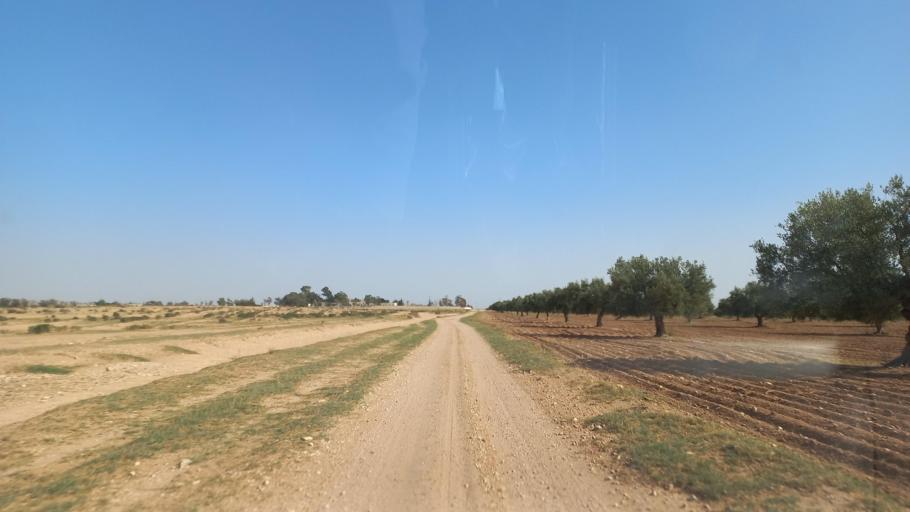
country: TN
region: Al Qasrayn
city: Kasserine
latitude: 35.3005
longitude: 9.0274
